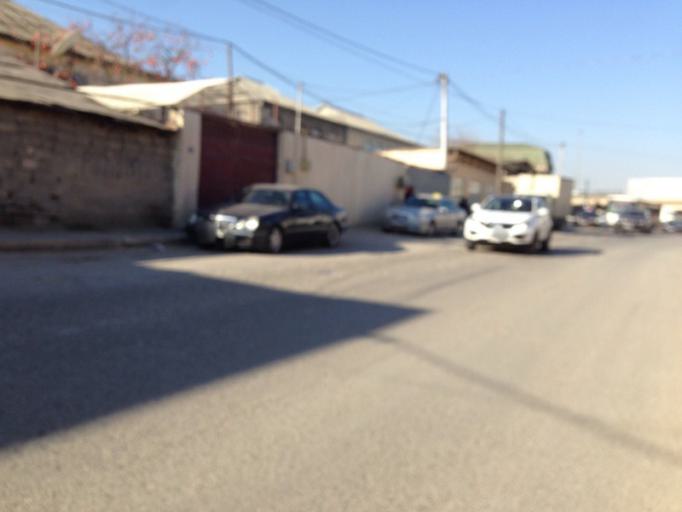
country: AZ
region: Baki
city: Baku
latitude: 40.4182
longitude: 49.8665
